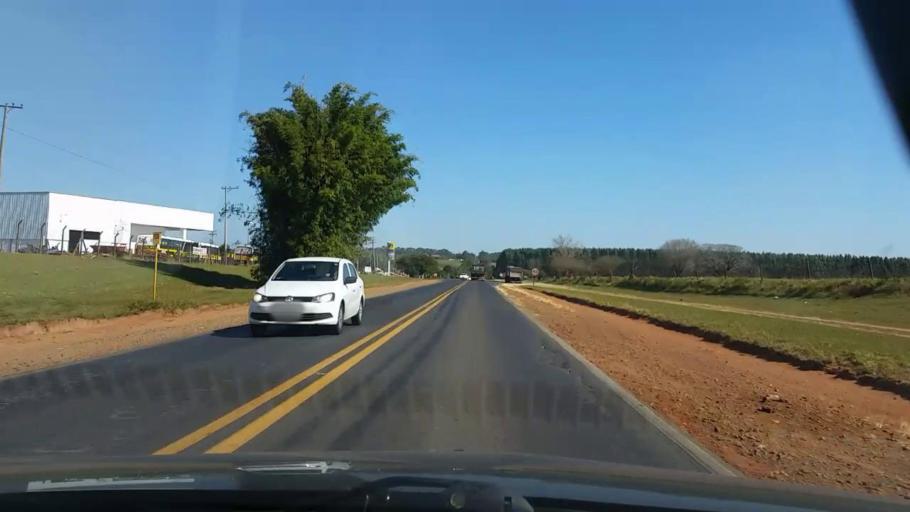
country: BR
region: Sao Paulo
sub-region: Sao Manuel
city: Sao Manuel
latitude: -22.8028
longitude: -48.6675
